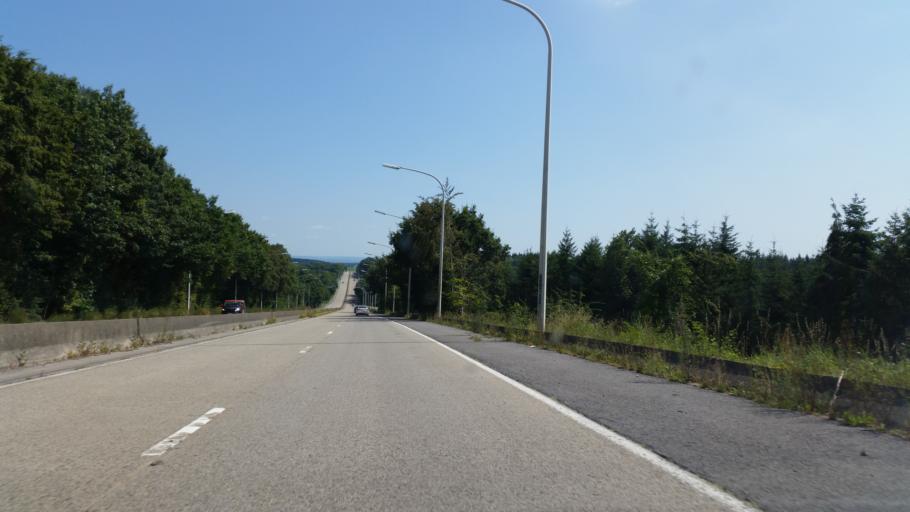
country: BE
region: Wallonia
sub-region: Province de Namur
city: Hamois
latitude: 50.2807
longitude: 5.1973
